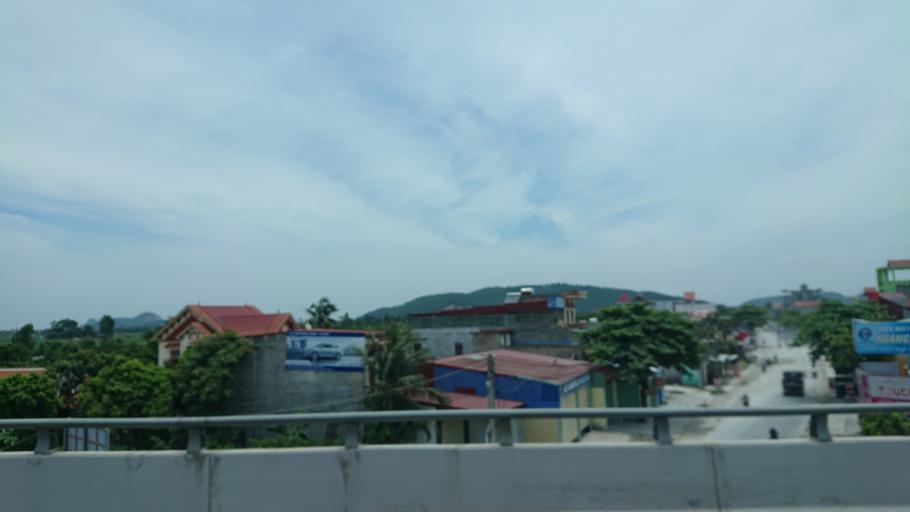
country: VN
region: Hai Phong
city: Nui Doi
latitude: 20.7708
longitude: 106.6101
